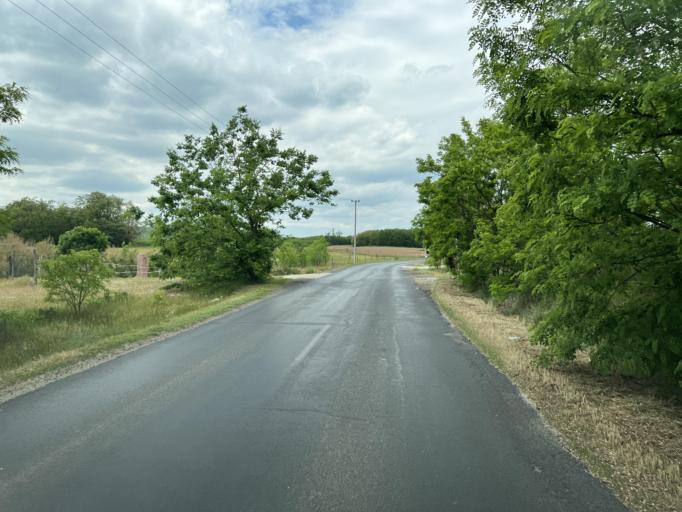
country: HU
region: Pest
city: Isaszeg
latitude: 47.5217
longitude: 19.4399
